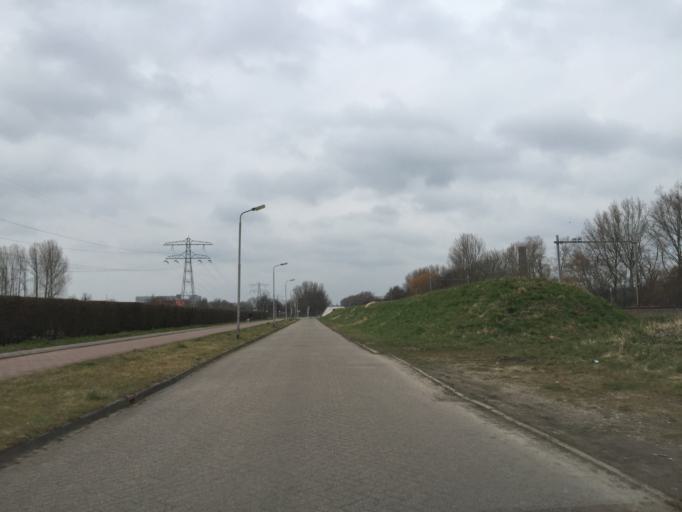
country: NL
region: South Holland
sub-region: Gemeente Delft
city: Delft
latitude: 51.9798
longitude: 4.3703
